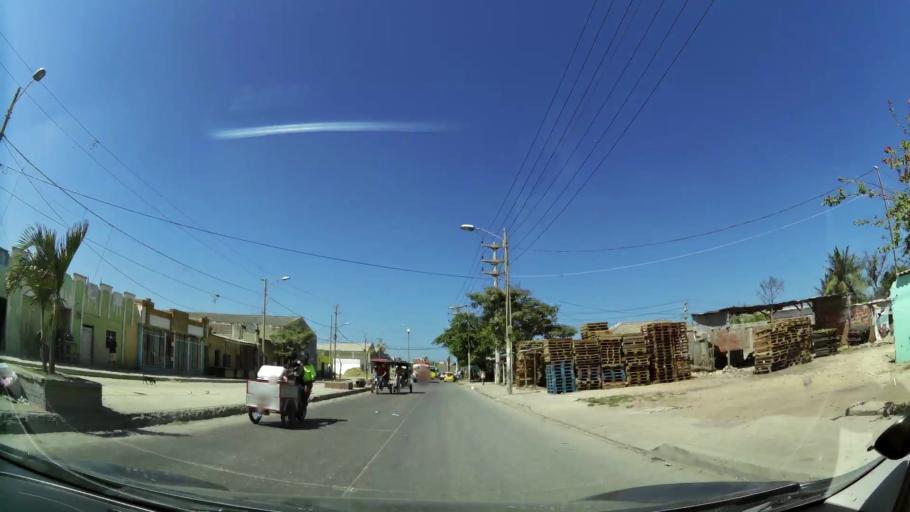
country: CO
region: Atlantico
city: Barranquilla
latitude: 10.9733
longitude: -74.7749
